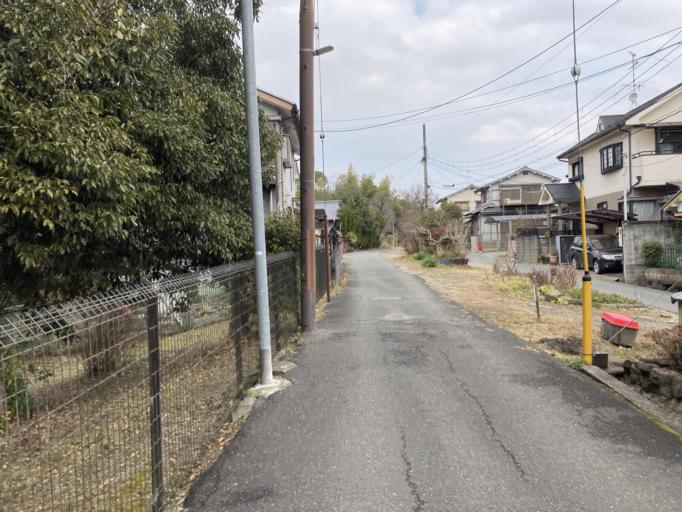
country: JP
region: Nara
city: Nara-shi
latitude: 34.6999
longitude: 135.7919
